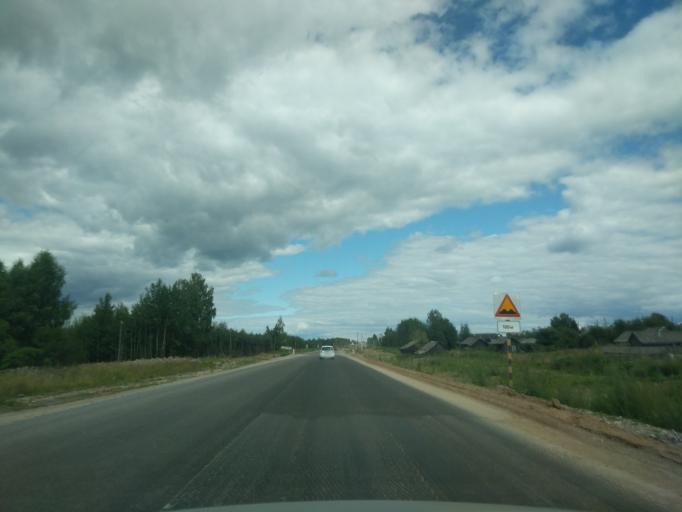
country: RU
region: Kostroma
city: Sudislavl'
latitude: 57.8629
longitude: 41.6215
